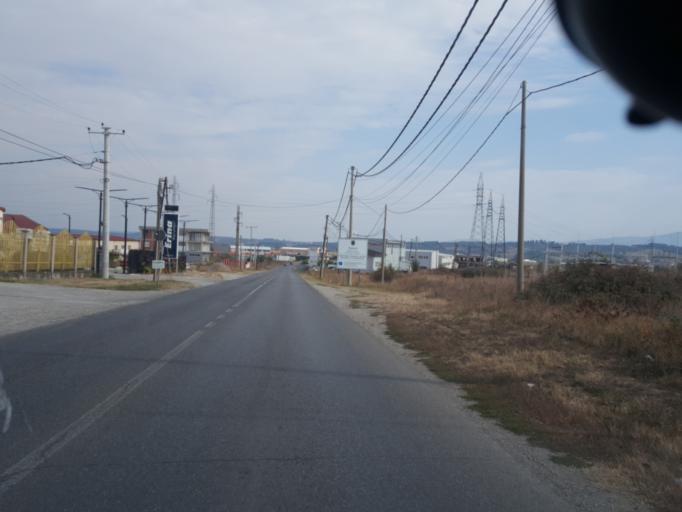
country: XK
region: Gjakova
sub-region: Komuna e Gjakoves
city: Gjakove
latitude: 42.3684
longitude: 20.4600
